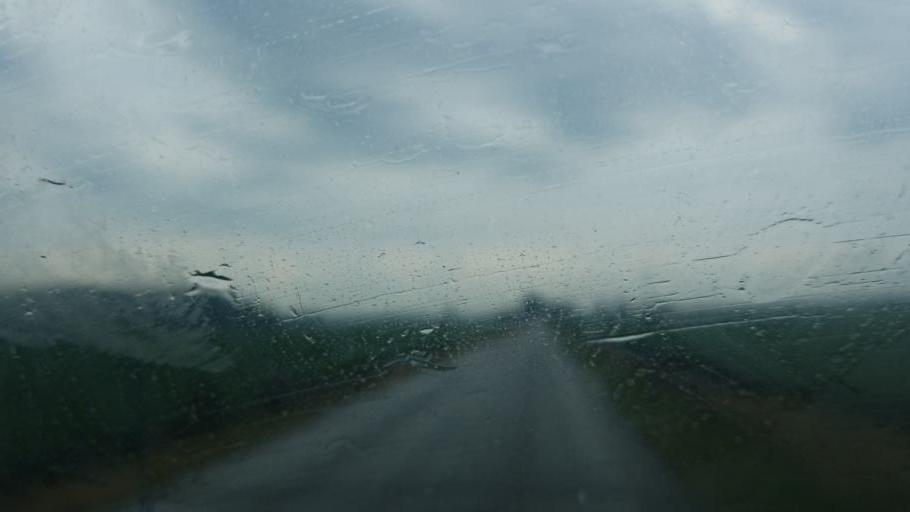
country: US
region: Indiana
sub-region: DeKalb County
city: Butler
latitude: 41.4730
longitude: -84.8608
